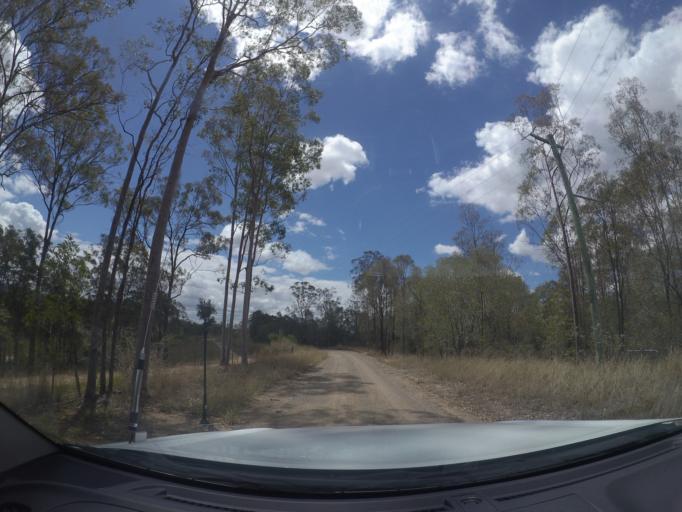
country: AU
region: Queensland
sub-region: Logan
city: Cedar Vale
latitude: -27.9138
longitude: 153.0534
